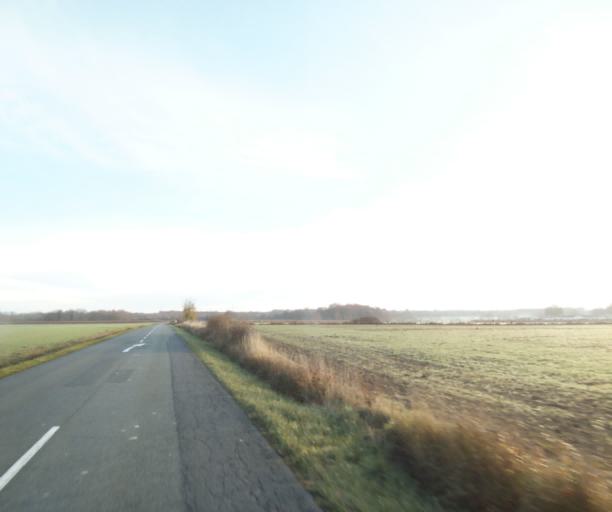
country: FR
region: Poitou-Charentes
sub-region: Departement de la Charente-Maritime
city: Fontcouverte
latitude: 45.7721
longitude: -0.5725
